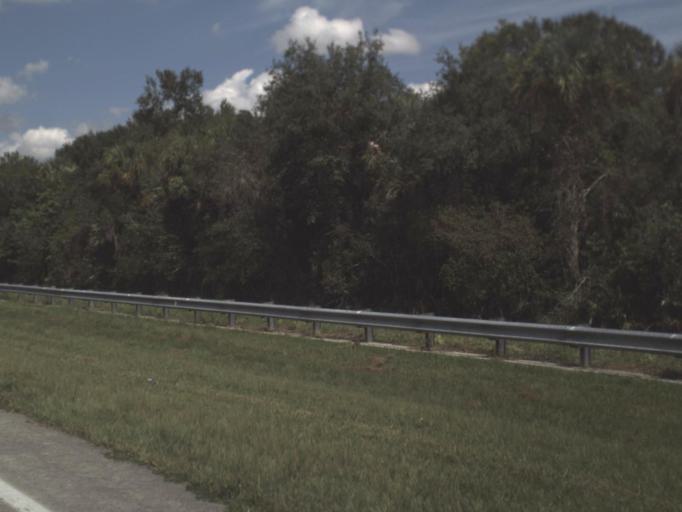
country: US
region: Florida
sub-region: Collier County
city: Orangetree
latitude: 26.1118
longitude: -81.3448
